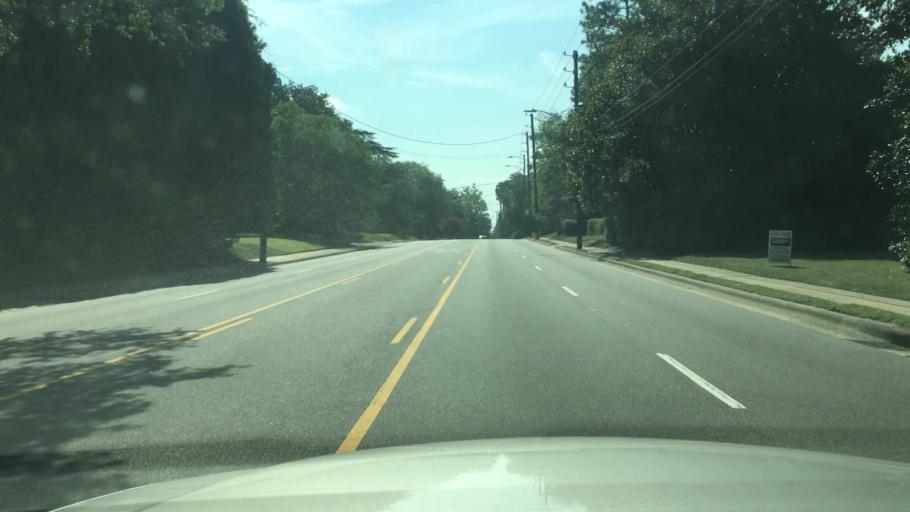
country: US
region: North Carolina
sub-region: Cumberland County
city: Fayetteville
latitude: 35.0585
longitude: -78.9064
